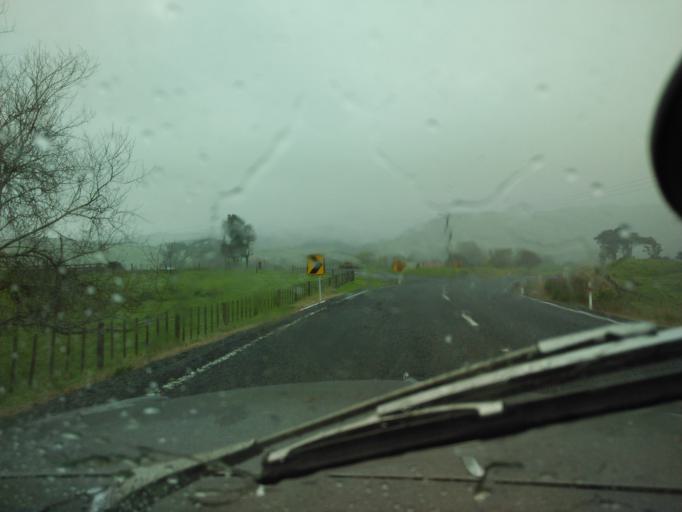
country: NZ
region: Auckland
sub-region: Auckland
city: Wellsford
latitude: -36.4016
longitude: 174.4484
